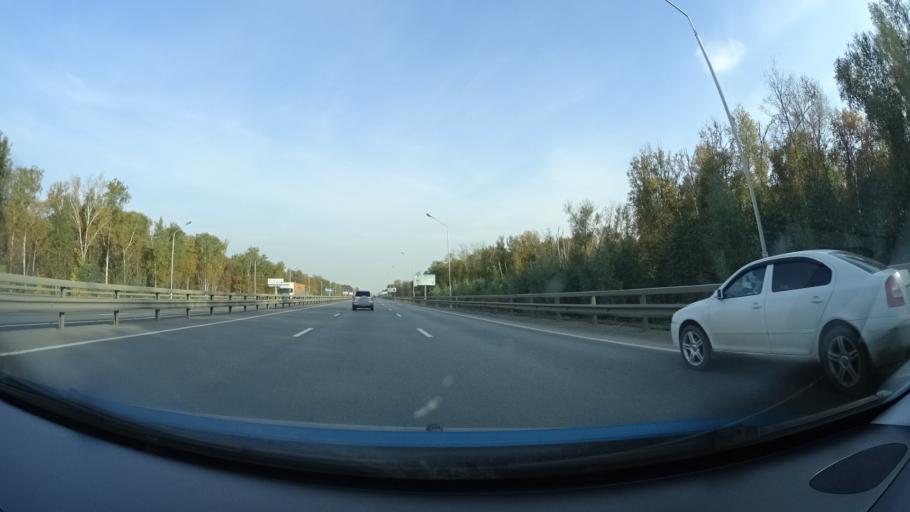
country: RU
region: Bashkortostan
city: Avdon
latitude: 54.6737
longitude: 55.8229
